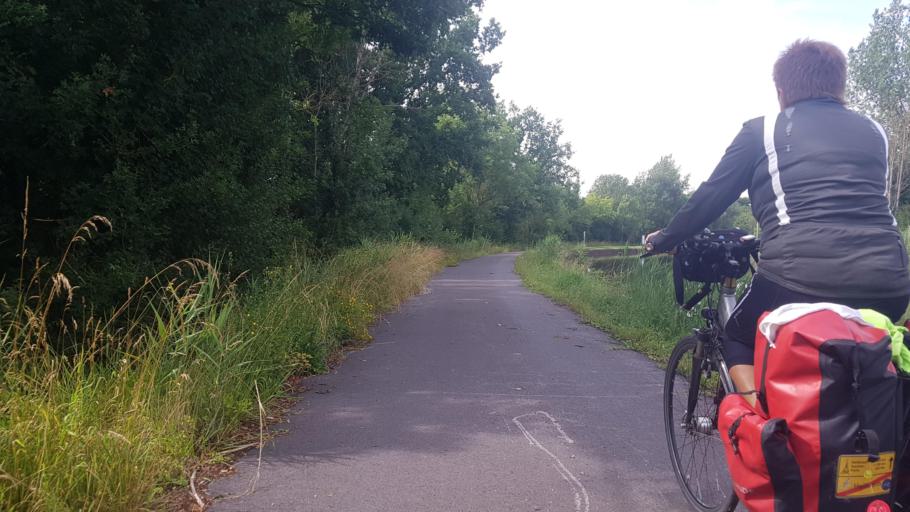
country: FR
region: Lorraine
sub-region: Departement de la Moselle
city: Dieuze
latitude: 48.6922
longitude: 6.7459
